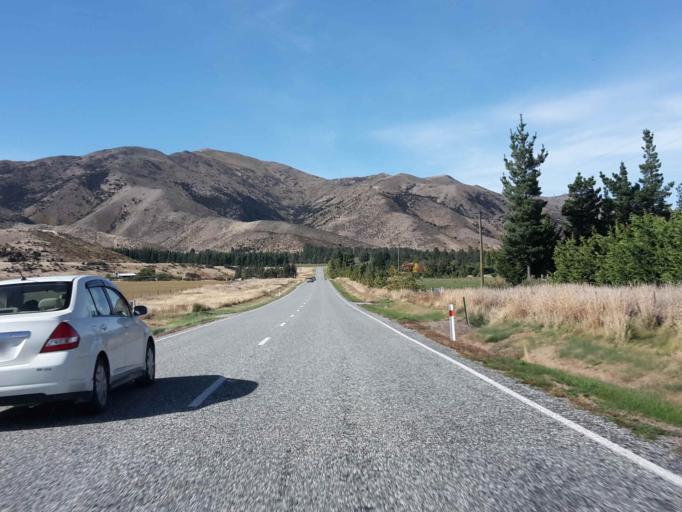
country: NZ
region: Otago
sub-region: Queenstown-Lakes District
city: Wanaka
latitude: -44.7395
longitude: 169.3286
